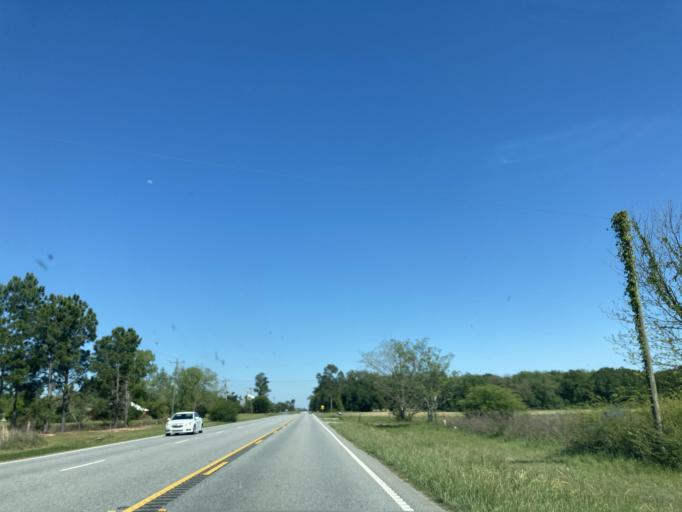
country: US
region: Georgia
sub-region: Miller County
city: Colquitt
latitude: 31.1855
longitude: -84.6088
